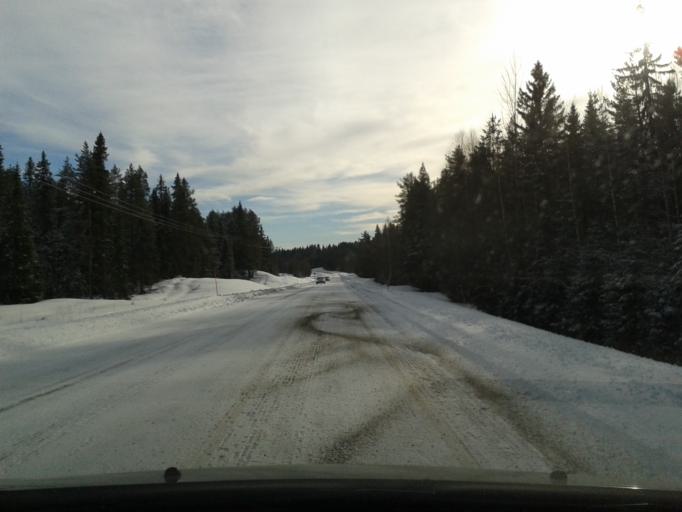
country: SE
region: Vaesterbotten
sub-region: Vilhelmina Kommun
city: Vilhelmina
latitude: 64.5441
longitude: 16.7459
